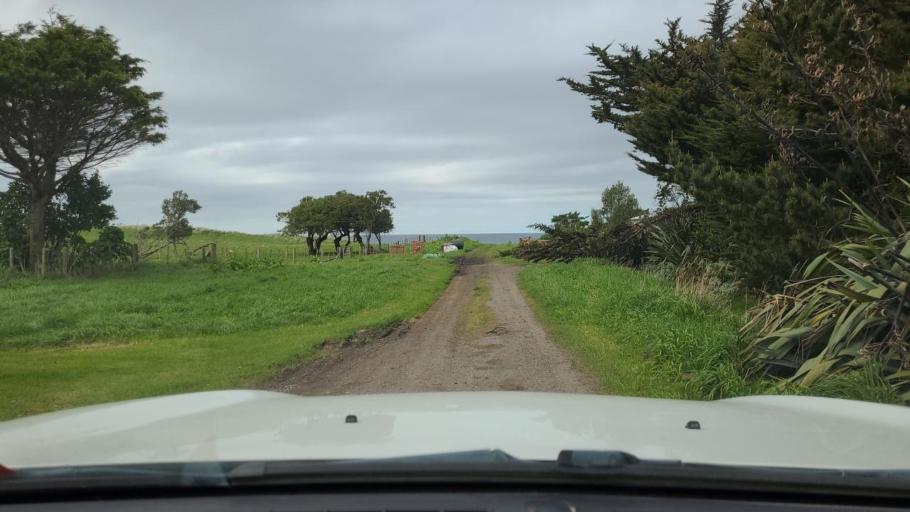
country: NZ
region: Chatham Islands
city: Waitangi
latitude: -44.0270
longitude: -176.3536
